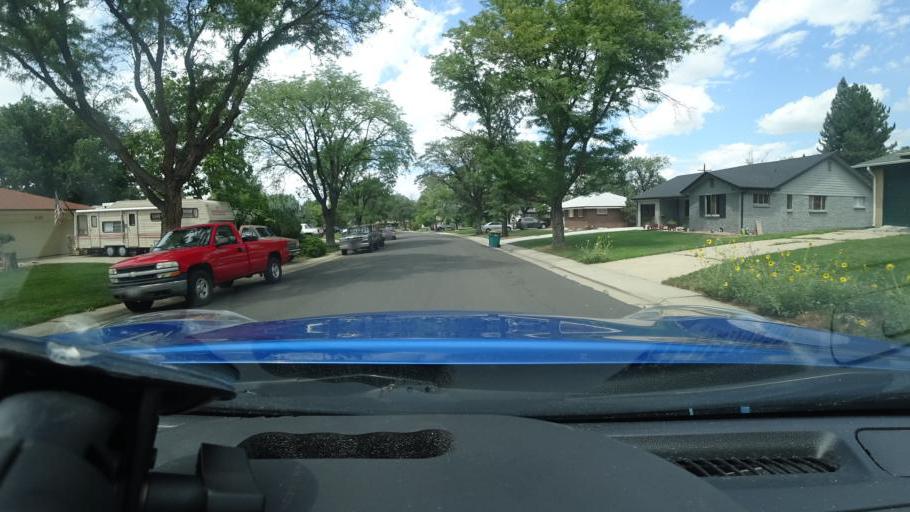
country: US
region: Colorado
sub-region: Adams County
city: Aurora
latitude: 39.7225
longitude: -104.8321
